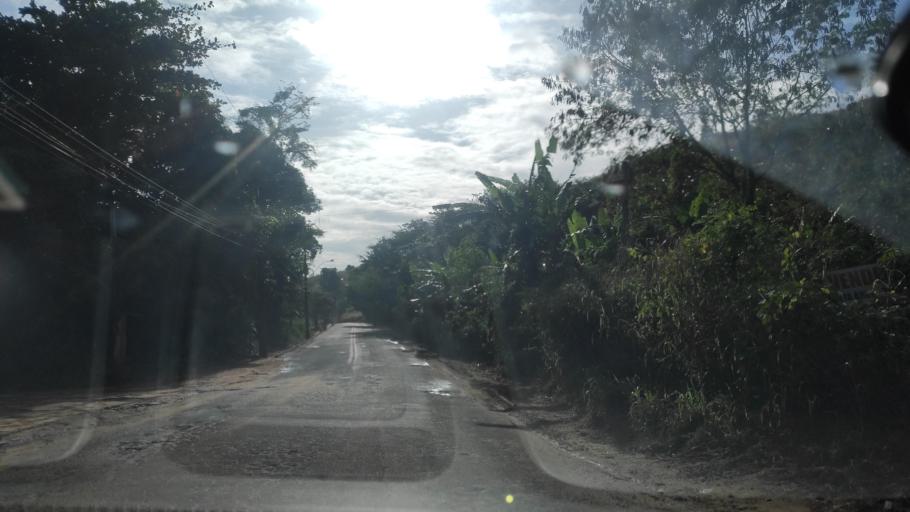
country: BR
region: Espirito Santo
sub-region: Nova Venecia
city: Nova Venecia
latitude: -18.7170
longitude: -40.3880
